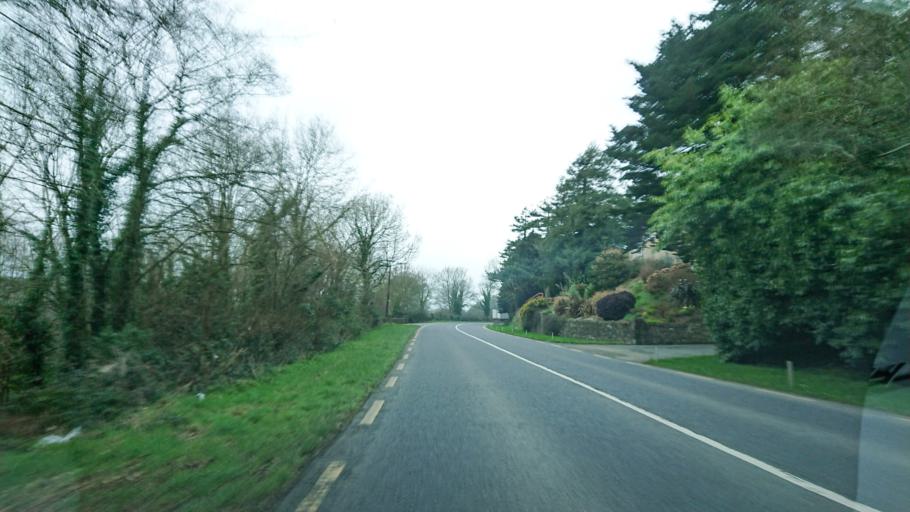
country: IE
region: Munster
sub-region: County Cork
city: Bandon
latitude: 51.7467
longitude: -8.7714
